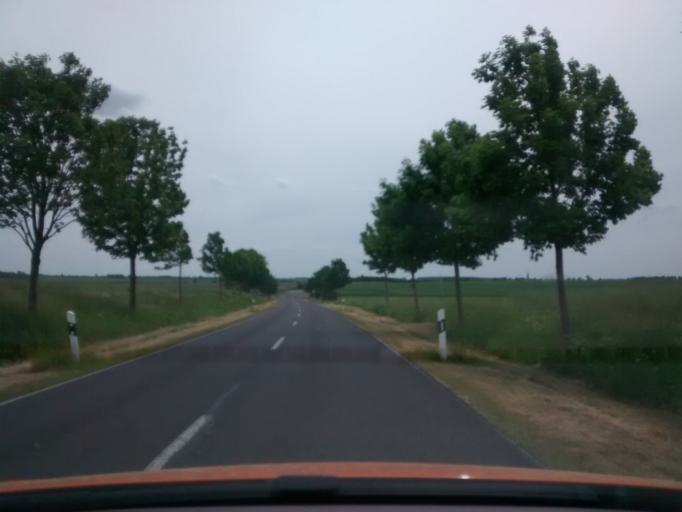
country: DE
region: Brandenburg
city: Juterbog
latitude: 51.9666
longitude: 13.0772
